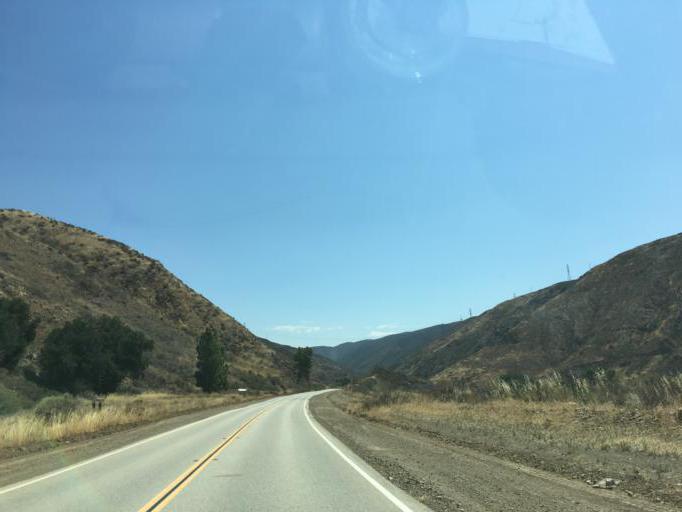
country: US
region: California
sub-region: Los Angeles County
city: Green Valley
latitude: 34.5675
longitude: -118.4728
